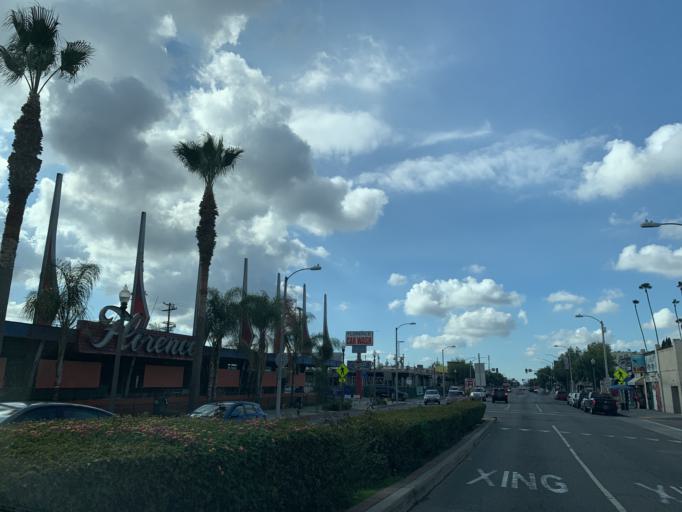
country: US
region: California
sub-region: Los Angeles County
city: Florence-Graham
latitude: 33.9748
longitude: -118.2436
